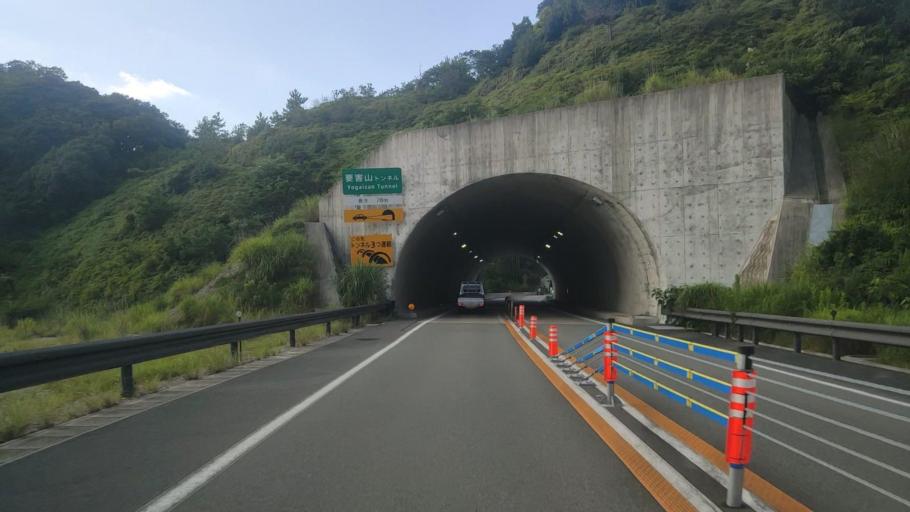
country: JP
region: Wakayama
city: Tanabe
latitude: 33.6383
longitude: 135.4098
